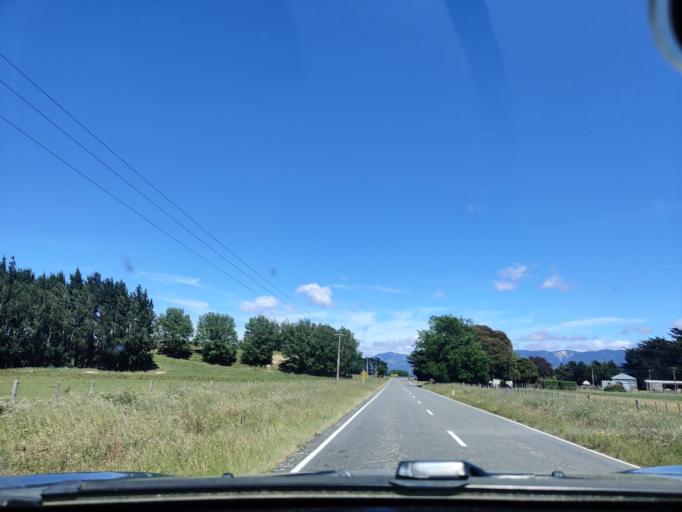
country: NZ
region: Wellington
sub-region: Upper Hutt City
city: Upper Hutt
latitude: -41.3280
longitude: 175.2155
